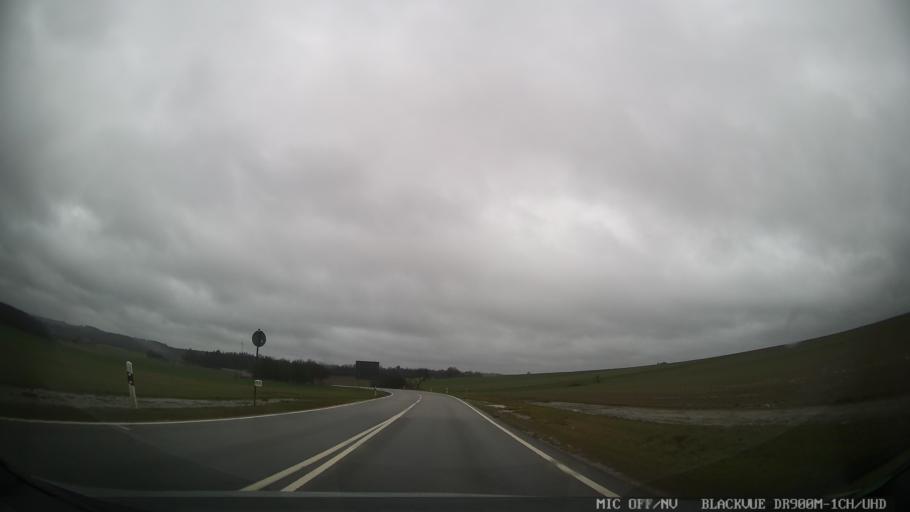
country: DE
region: Rheinland-Pfalz
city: Kirf
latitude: 49.5153
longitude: 6.4529
